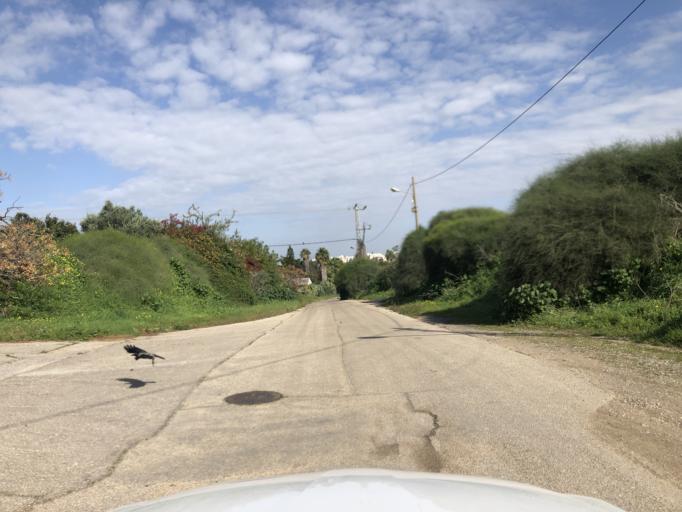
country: IL
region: Central District
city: Ness Ziona
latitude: 31.9158
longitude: 34.7961
